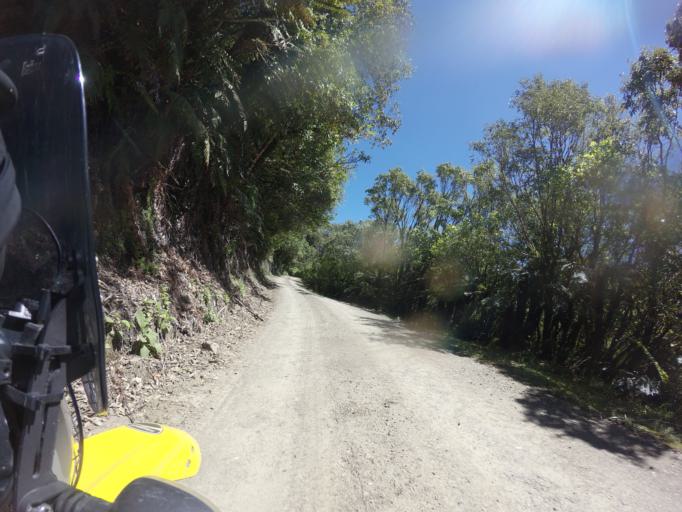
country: NZ
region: Bay of Plenty
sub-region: Opotiki District
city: Opotiki
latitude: -38.4084
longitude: 177.4236
